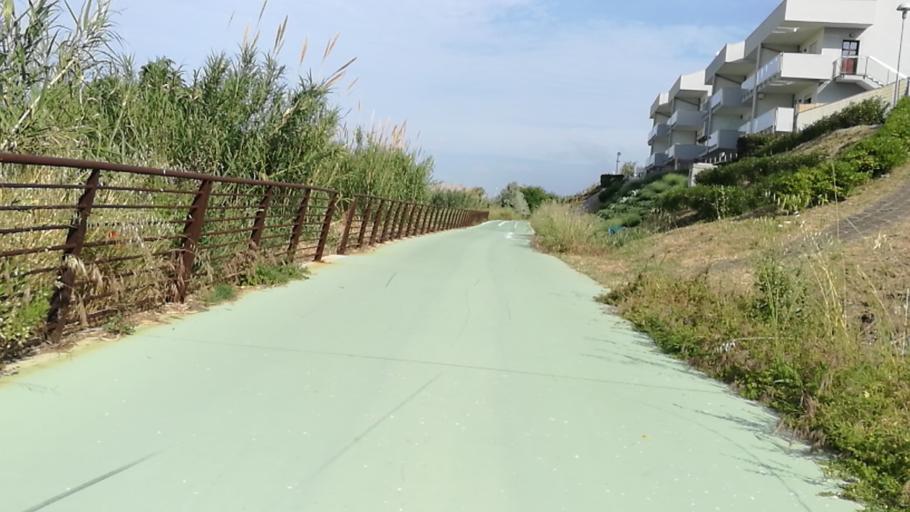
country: IT
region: Abruzzo
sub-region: Provincia di Chieti
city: Torino di Sangro
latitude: 42.2105
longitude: 14.5911
